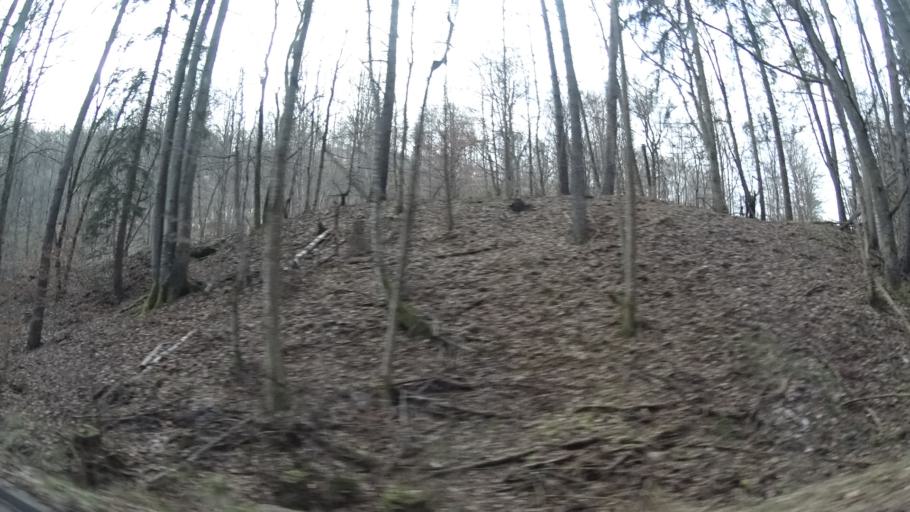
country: DE
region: Baden-Wuerttemberg
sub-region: Regierungsbezirk Stuttgart
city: Gerlingen
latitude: 48.7705
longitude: 9.0551
